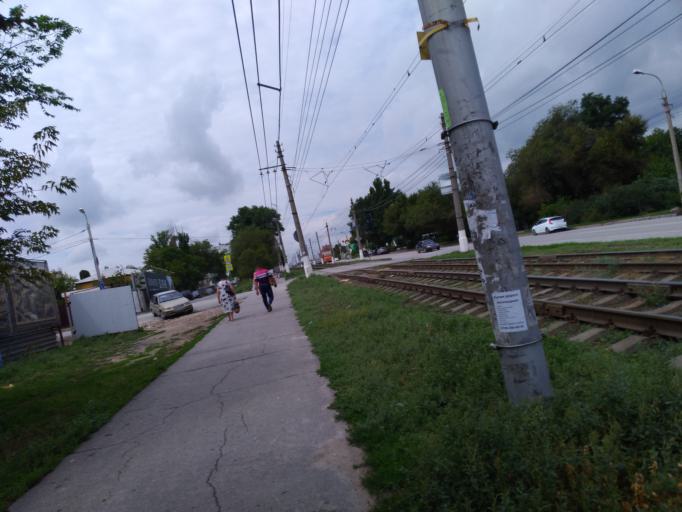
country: RU
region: Volgograd
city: Volgograd
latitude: 48.7146
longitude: 44.4941
